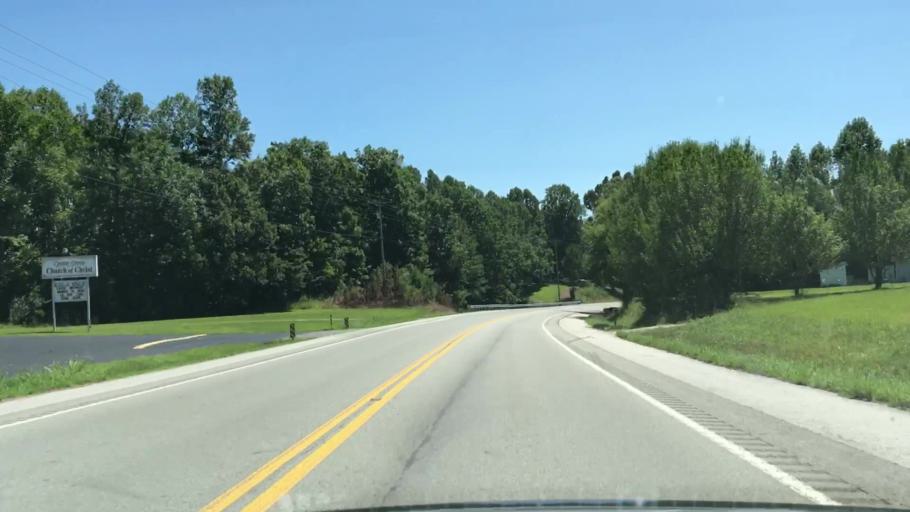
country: US
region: Tennessee
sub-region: Jackson County
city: Dodson Branch
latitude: 36.2634
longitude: -85.6118
